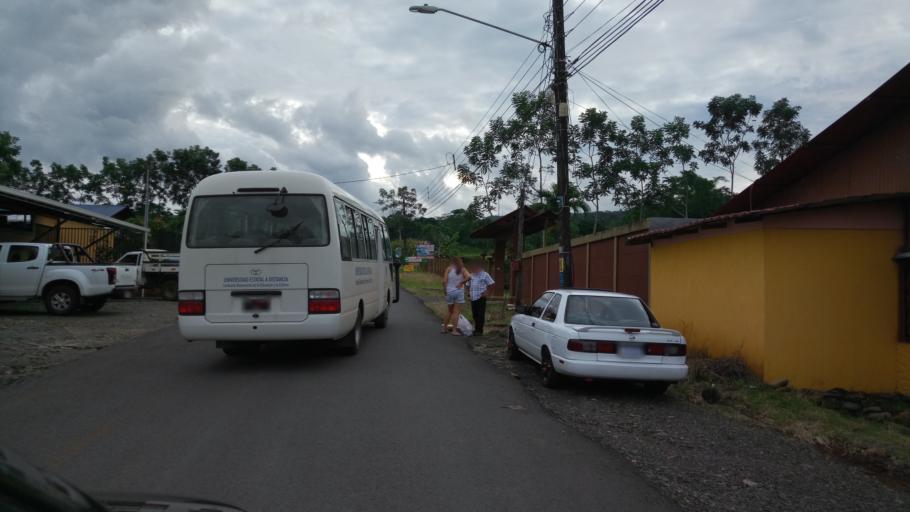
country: CR
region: Alajuela
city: Pocosol
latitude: 10.3403
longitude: -84.5818
